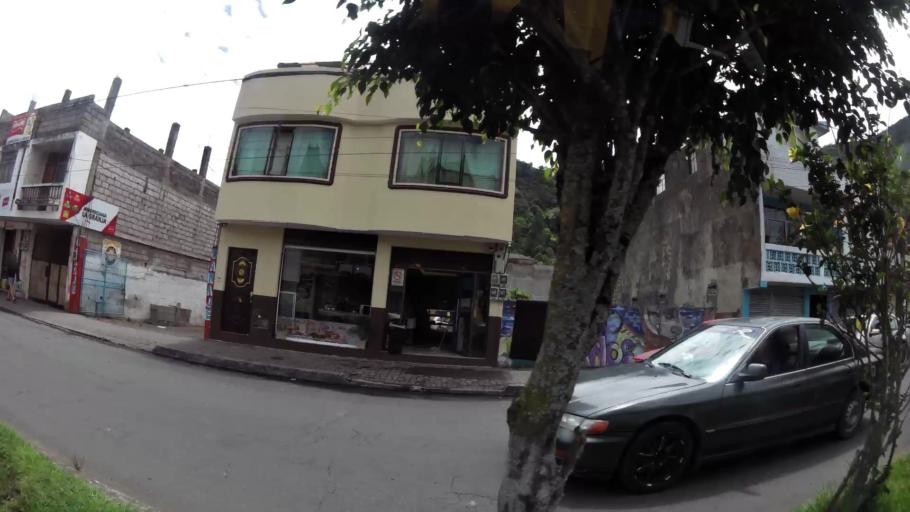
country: EC
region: Tungurahua
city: Banos
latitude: -1.3944
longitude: -78.4200
